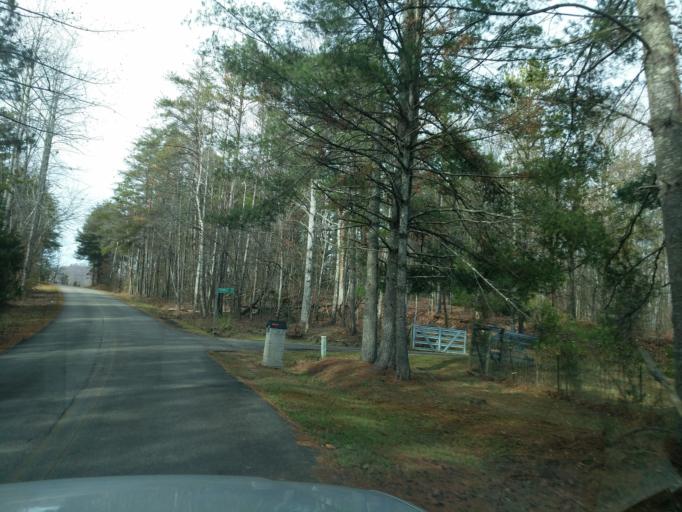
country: US
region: South Carolina
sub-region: Oconee County
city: Walhalla
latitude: 34.8581
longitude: -83.0548
